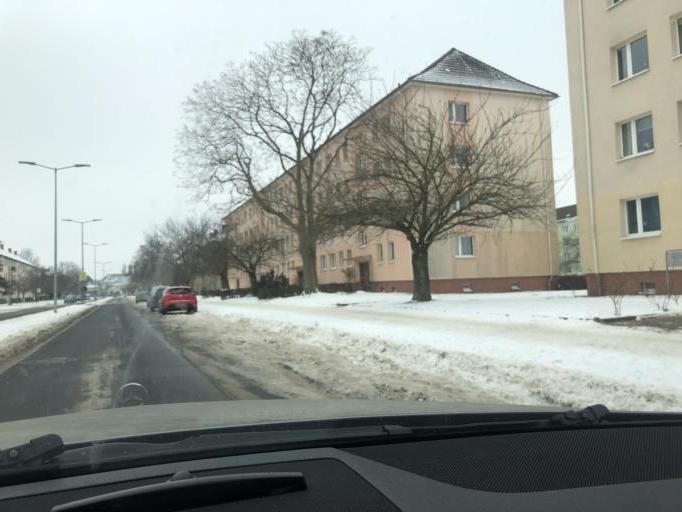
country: DE
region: Brandenburg
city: Guben
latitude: 51.9469
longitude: 14.7036
